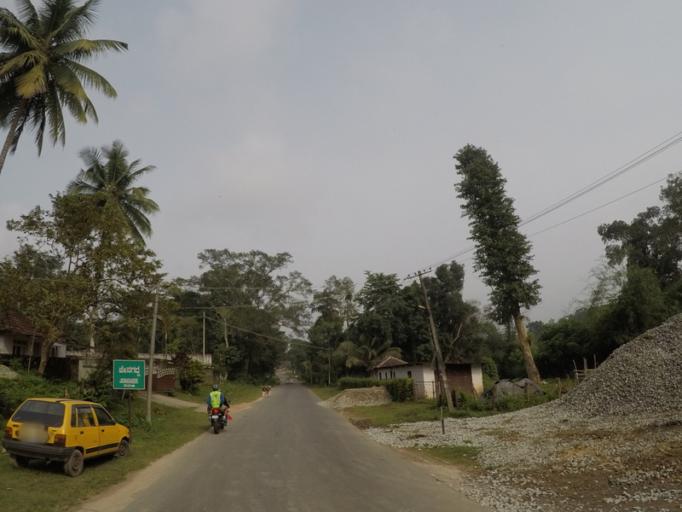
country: IN
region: Karnataka
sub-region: Chikmagalur
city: Chikmagalur
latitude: 13.3375
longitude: 75.5487
